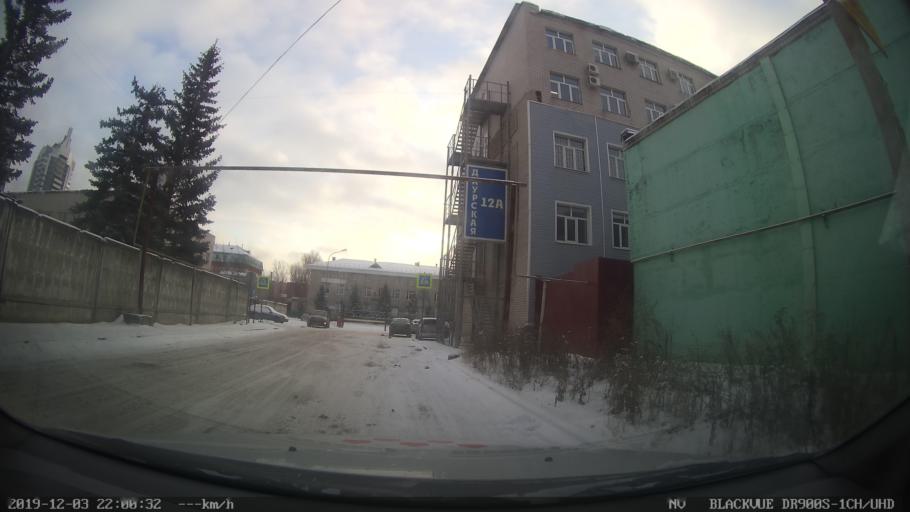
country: RU
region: Tatarstan
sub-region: Gorod Kazan'
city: Kazan
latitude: 55.7612
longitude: 49.1459
